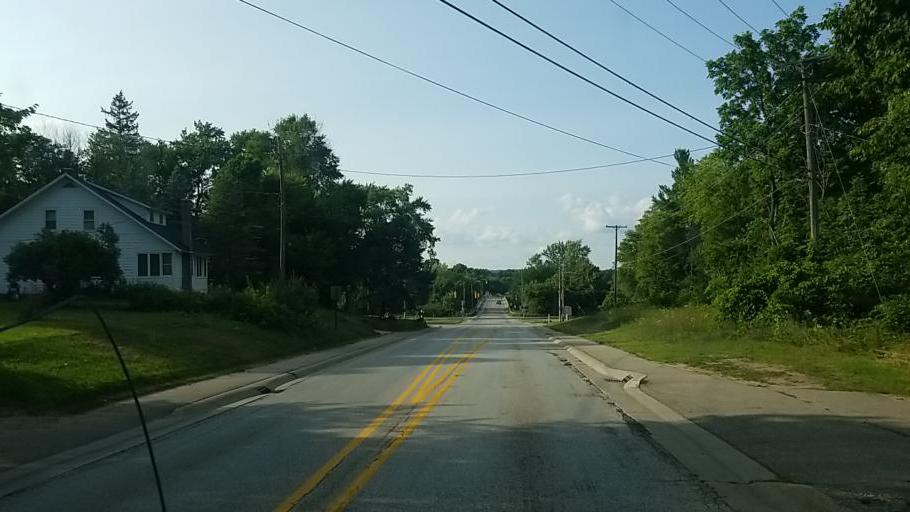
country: US
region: Michigan
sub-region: Kent County
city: Lowell
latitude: 42.9227
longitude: -85.3424
